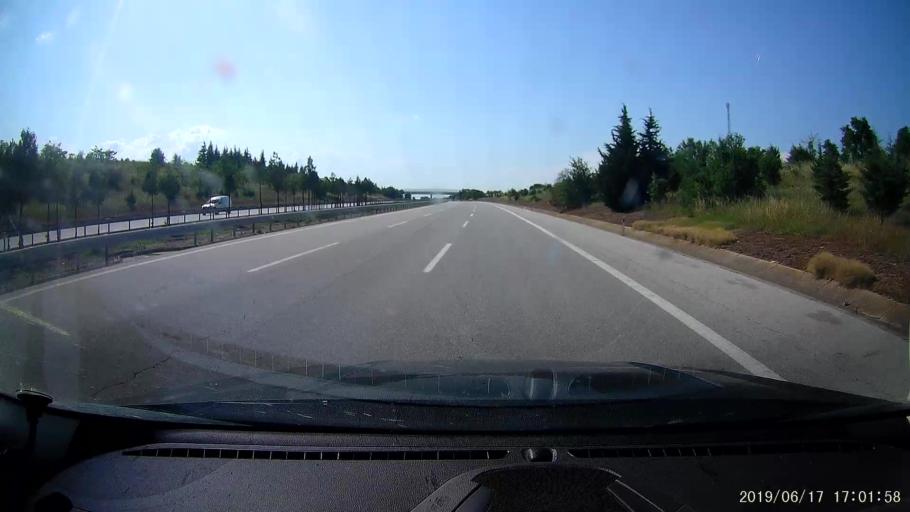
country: TR
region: Edirne
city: Haskoy
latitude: 41.6345
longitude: 26.7920
